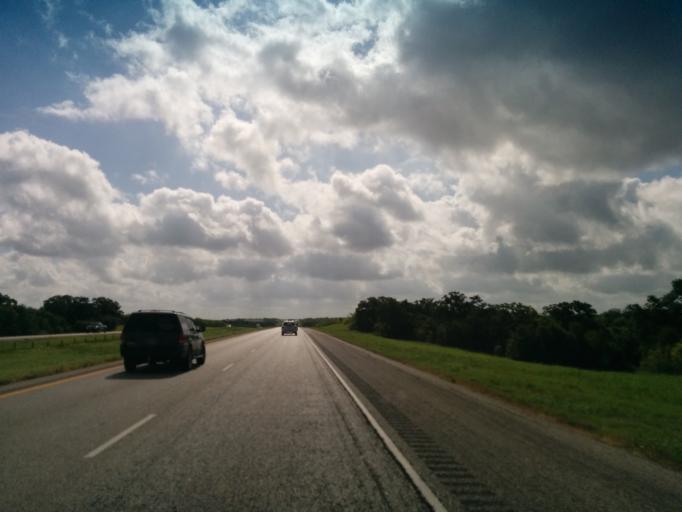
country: US
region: Texas
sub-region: Gonzales County
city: Waelder
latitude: 29.6646
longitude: -97.3574
